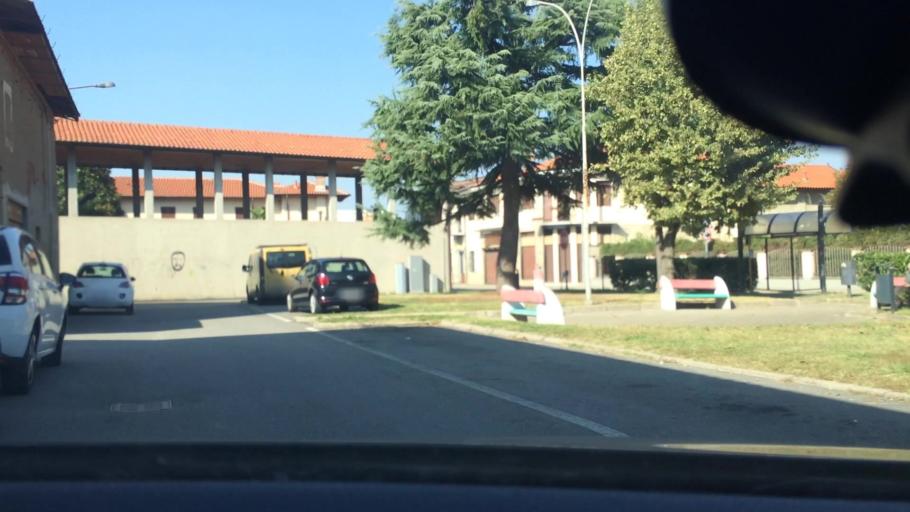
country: IT
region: Lombardy
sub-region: Citta metropolitana di Milano
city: Casate
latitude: 45.4931
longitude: 8.8280
